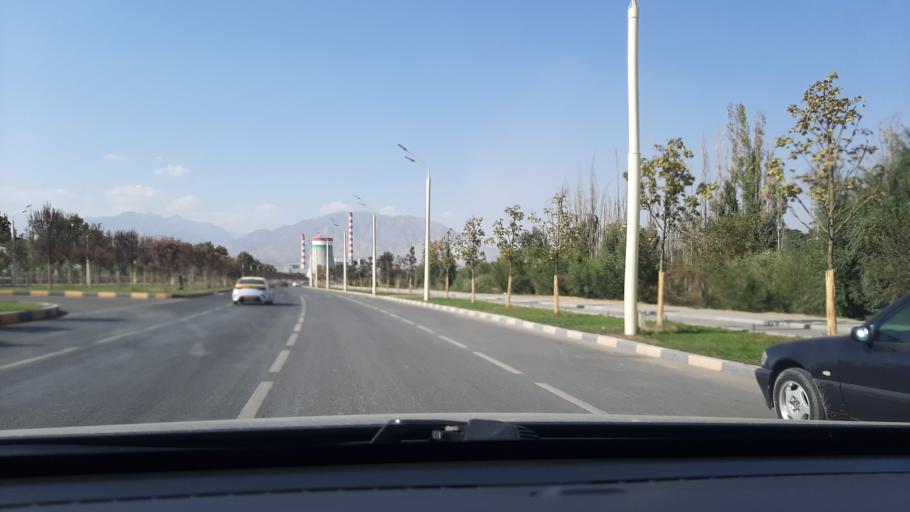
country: TJ
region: Dushanbe
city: Dushanbe
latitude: 38.5956
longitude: 68.7769
